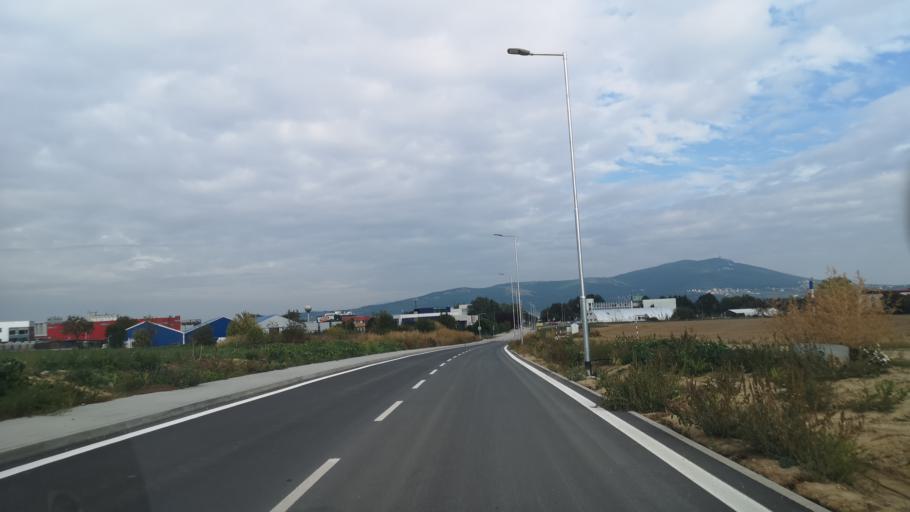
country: SK
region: Nitriansky
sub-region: Okres Nitra
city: Nitra
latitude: 48.3243
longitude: 18.0240
